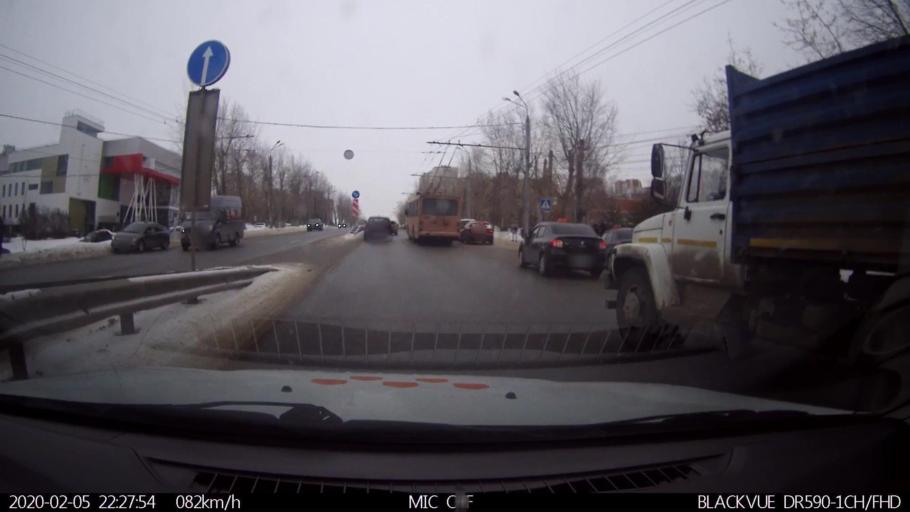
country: RU
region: Nizjnij Novgorod
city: Imeni Stepana Razina
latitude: 54.7611
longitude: 44.1233
